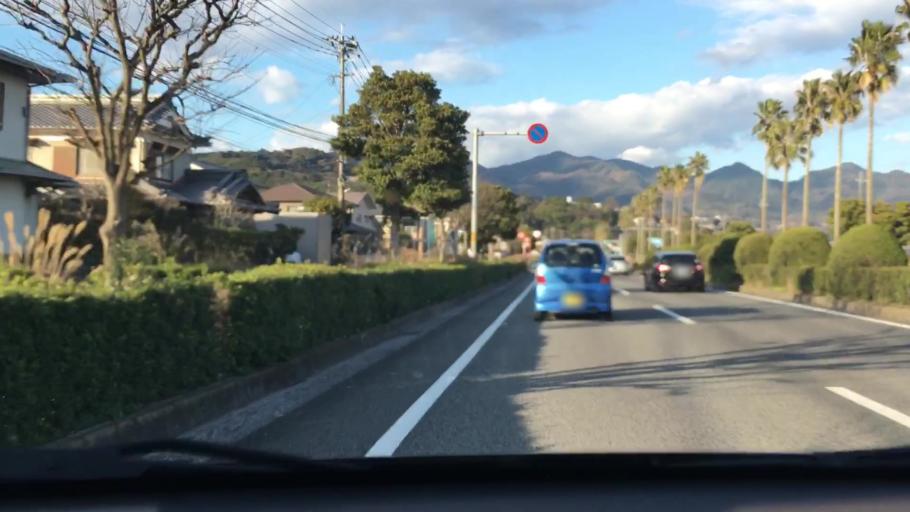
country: JP
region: Oita
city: Hiji
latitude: 33.3398
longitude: 131.4943
